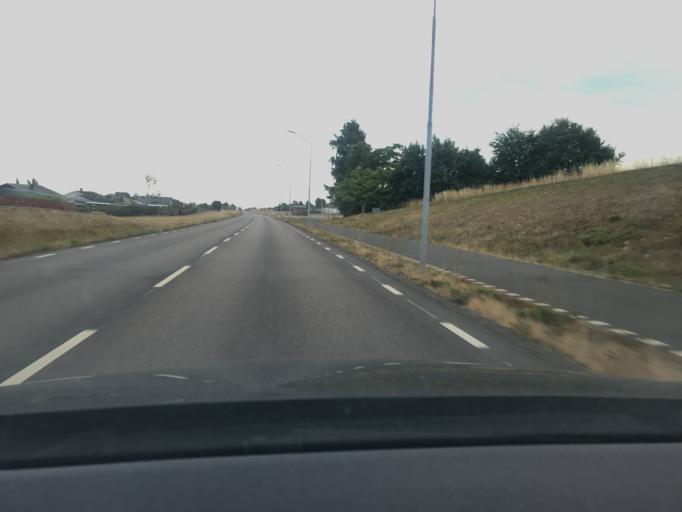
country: SE
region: Skane
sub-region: Simrishamns Kommun
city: Simrishamn
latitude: 55.5478
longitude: 14.3503
